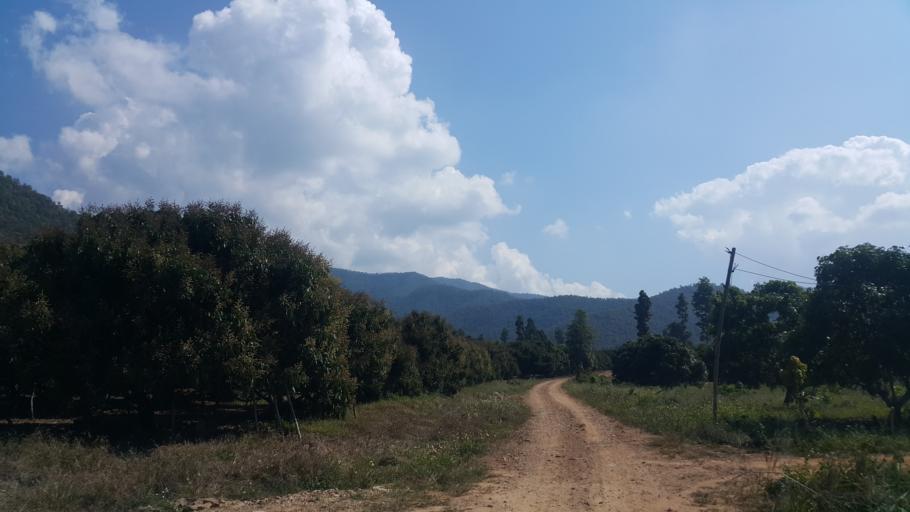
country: TH
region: Lamphun
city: Ban Thi
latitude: 18.6741
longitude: 99.1758
